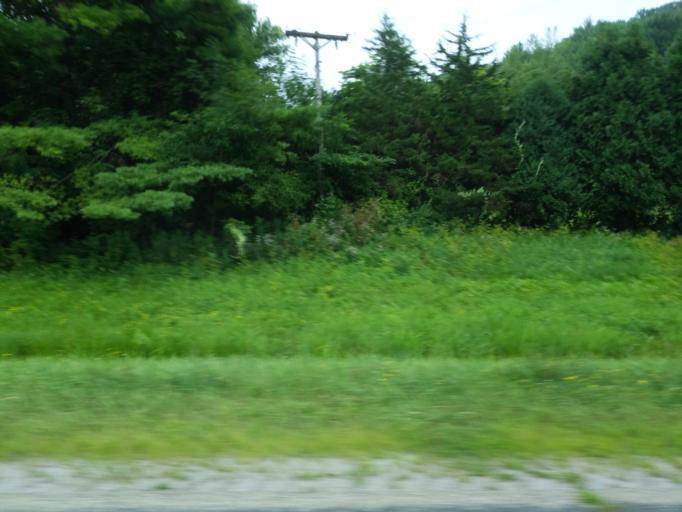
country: US
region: Wisconsin
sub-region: Sauk County
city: Sauk City
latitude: 43.2363
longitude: -89.7305
